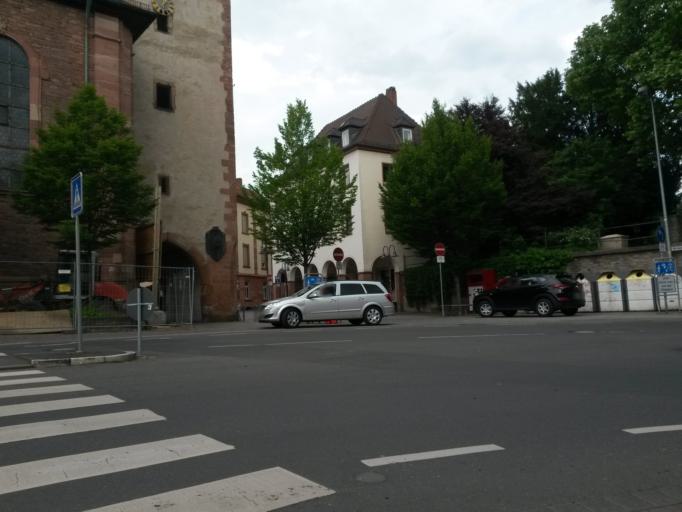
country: DE
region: Bavaria
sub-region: Regierungsbezirk Unterfranken
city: Aschaffenburg
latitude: 49.9740
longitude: 9.1512
